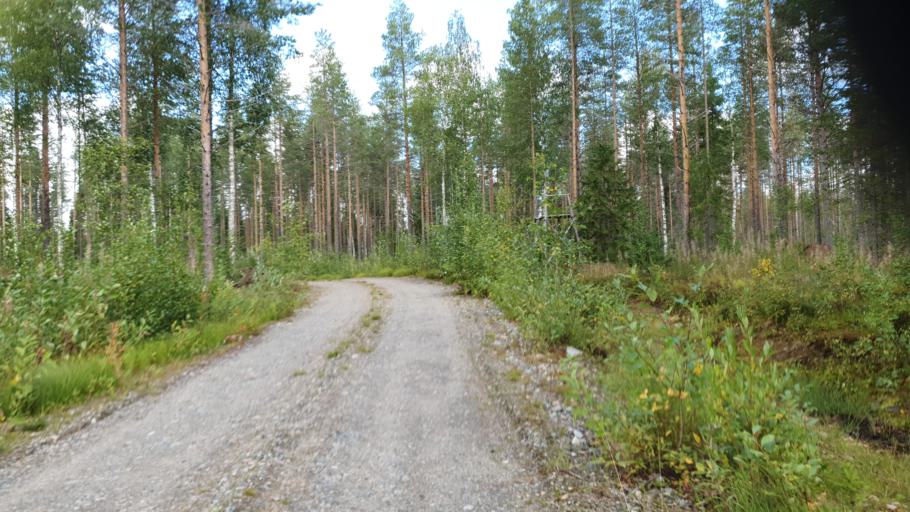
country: FI
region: Kainuu
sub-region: Kehys-Kainuu
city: Kuhmo
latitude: 64.1426
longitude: 29.3872
